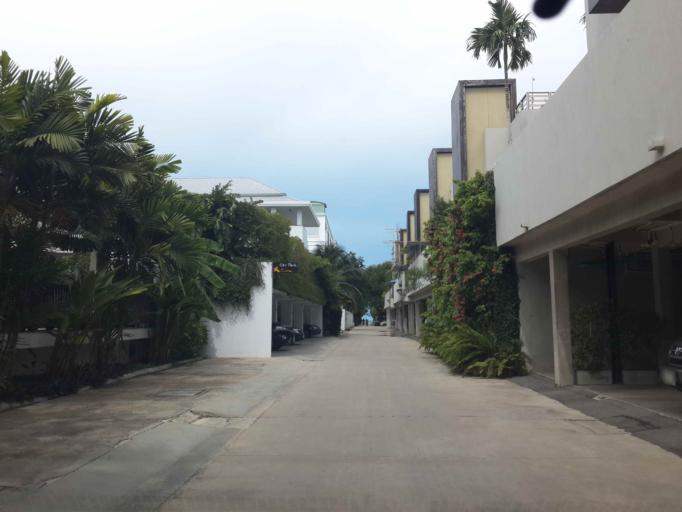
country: TH
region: Prachuap Khiri Khan
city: Hua Hin
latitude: 12.5310
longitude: 99.9695
